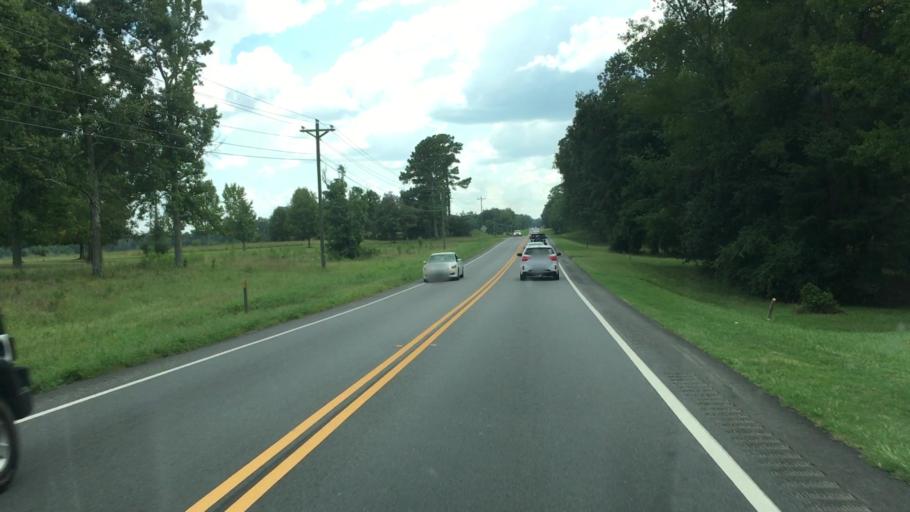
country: US
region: Georgia
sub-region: Putnam County
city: Eatonton
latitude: 33.3733
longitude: -83.3809
